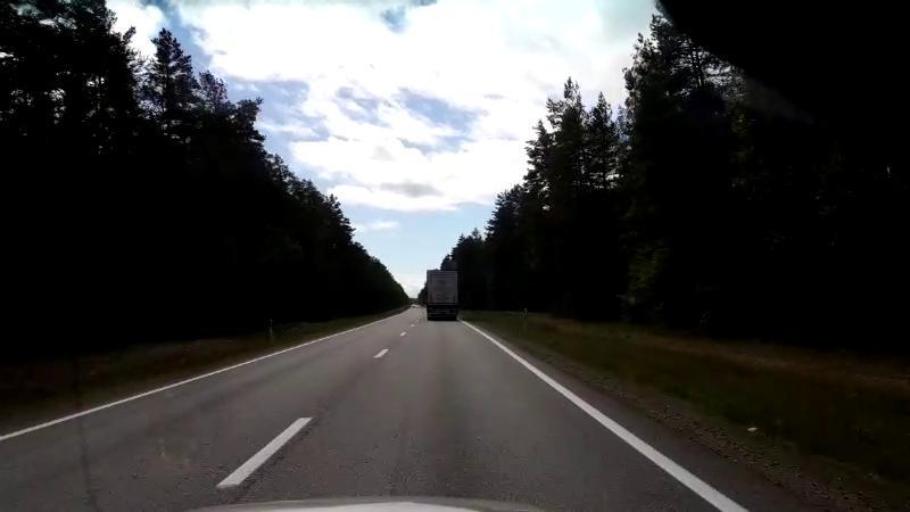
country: LV
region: Salacgrivas
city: Salacgriva
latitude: 57.5271
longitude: 24.4308
